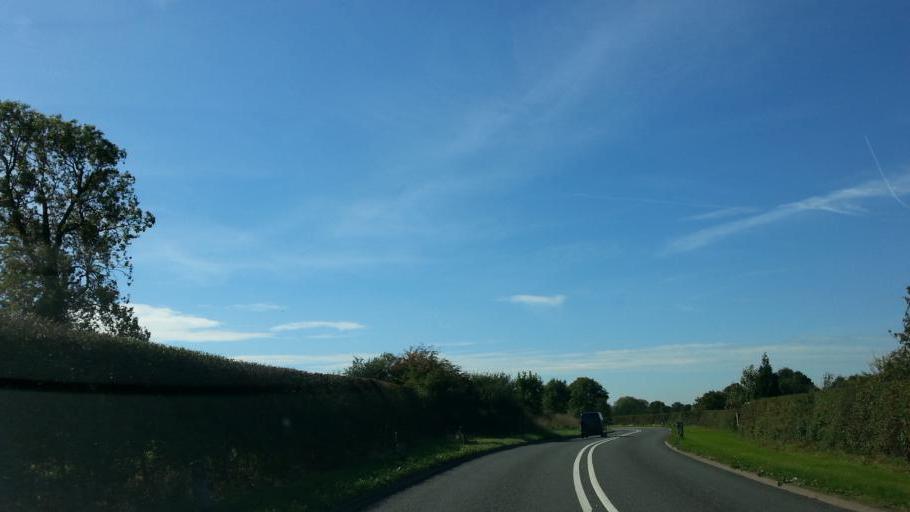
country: GB
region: England
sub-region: Staffordshire
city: Colwich
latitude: 52.8488
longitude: -1.9969
